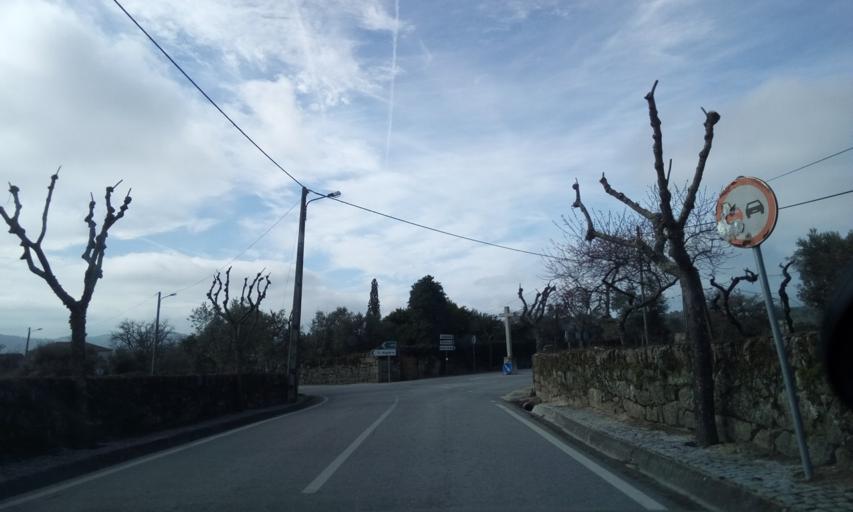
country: PT
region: Guarda
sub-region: Aguiar da Beira
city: Aguiar da Beira
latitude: 40.7352
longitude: -7.5565
